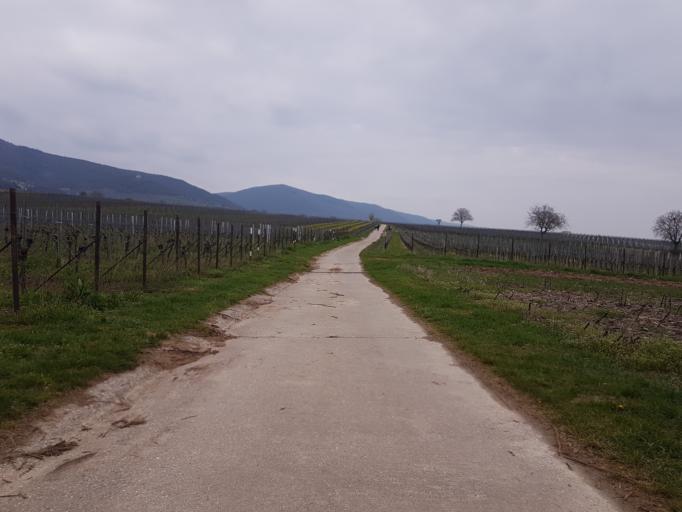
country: DE
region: Rheinland-Pfalz
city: Bochingen
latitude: 49.2296
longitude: 8.0797
